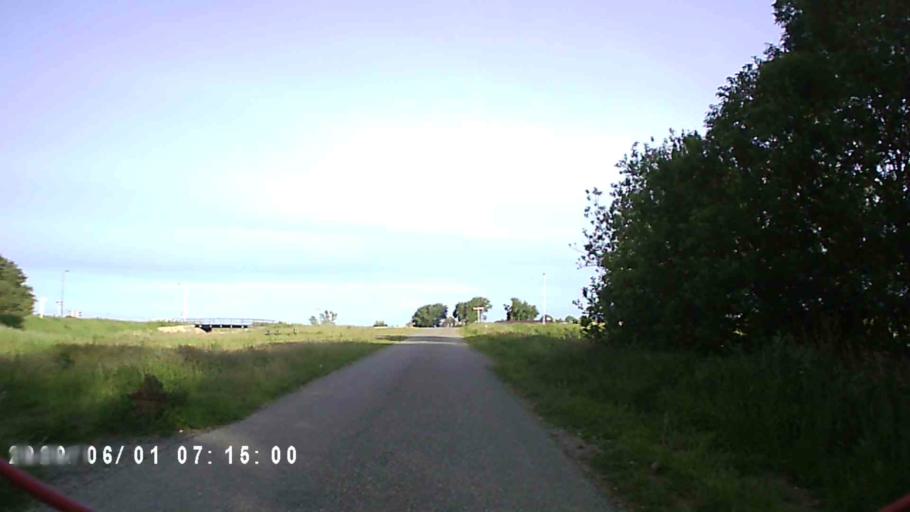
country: NL
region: Friesland
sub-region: Gemeente Dantumadiel
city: Walterswald
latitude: 53.3142
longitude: 6.0482
